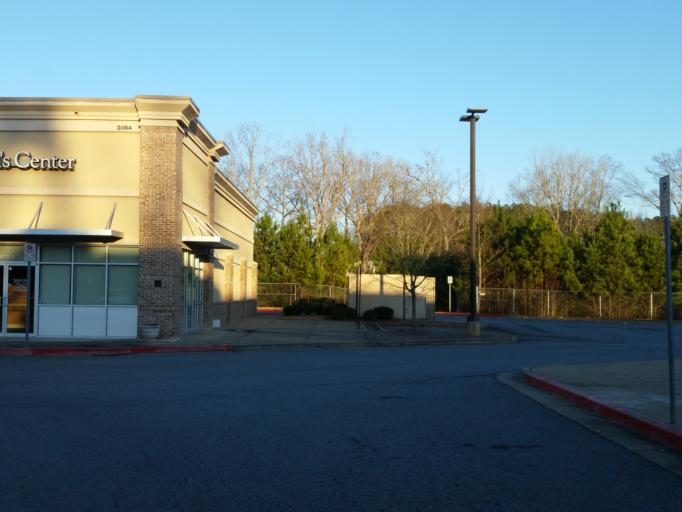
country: US
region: Georgia
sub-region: Cherokee County
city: Holly Springs
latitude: 34.1738
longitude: -84.4189
